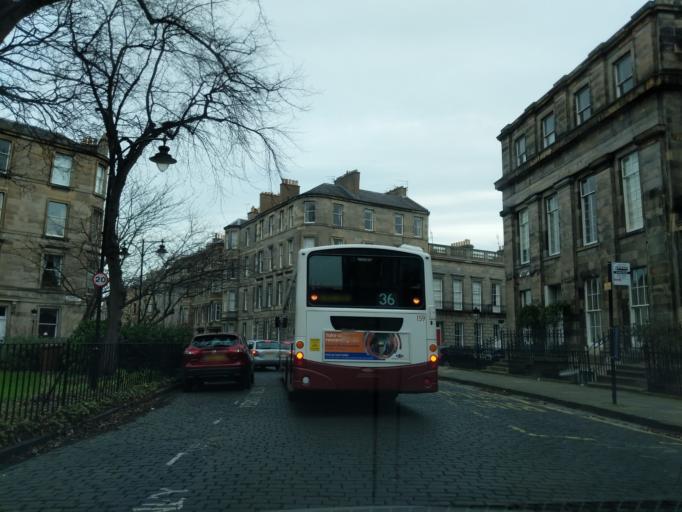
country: GB
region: Scotland
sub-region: Edinburgh
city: Edinburgh
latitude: 55.9574
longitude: -3.2119
